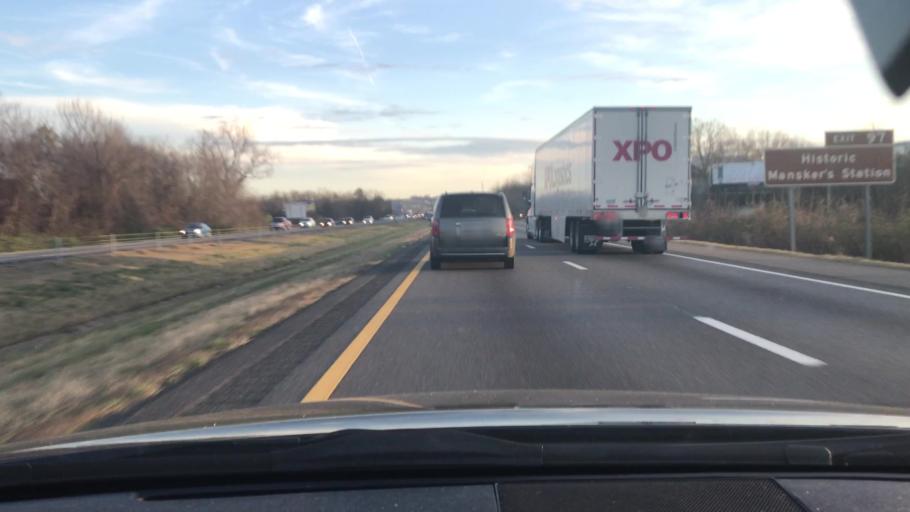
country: US
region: Tennessee
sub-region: Davidson County
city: Goodlettsville
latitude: 36.3368
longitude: -86.7116
